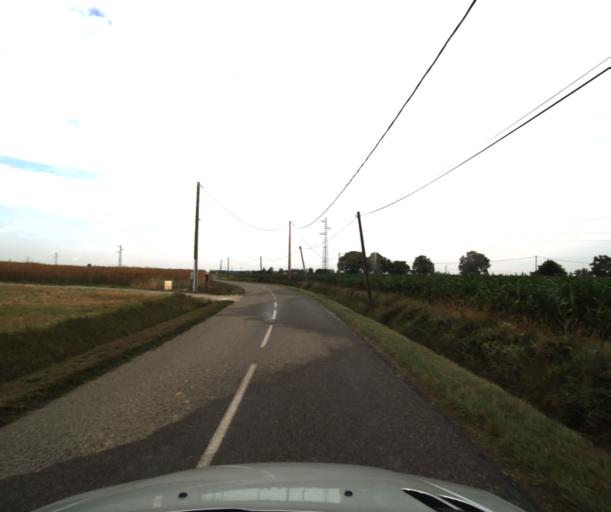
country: FR
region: Midi-Pyrenees
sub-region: Departement de la Haute-Garonne
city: Lacasse
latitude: 43.4241
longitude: 1.2704
